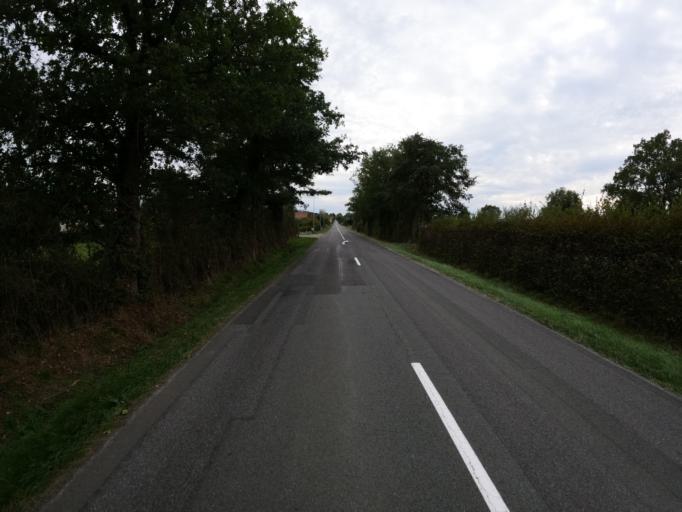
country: FR
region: Poitou-Charentes
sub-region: Departement de la Vienne
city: Saulge
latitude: 46.3570
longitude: 0.8348
